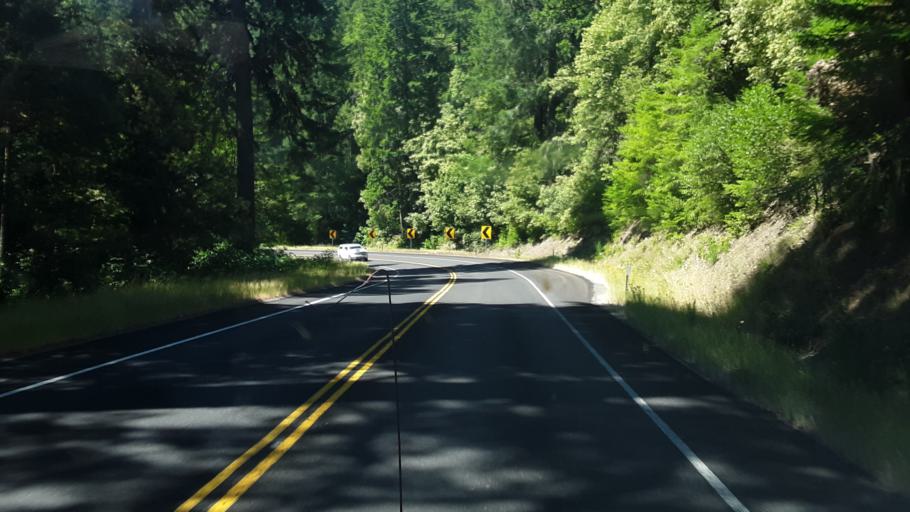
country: US
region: Oregon
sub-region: Josephine County
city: Cave Junction
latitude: 41.9347
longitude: -123.7564
